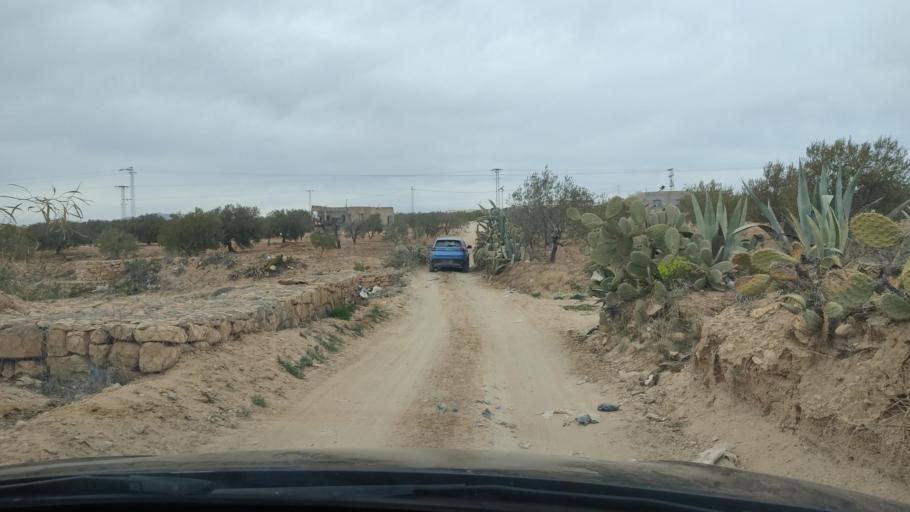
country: TN
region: Al Qasrayn
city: Kasserine
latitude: 35.2300
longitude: 8.9111
